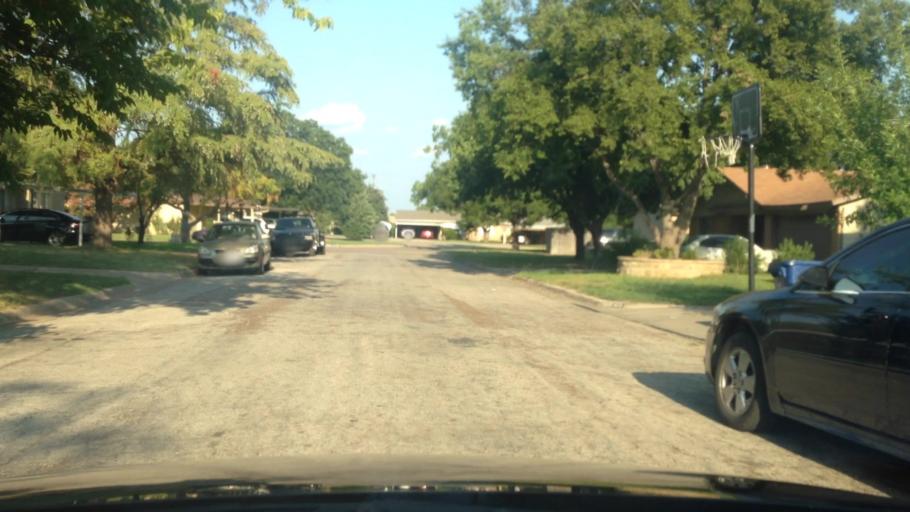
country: US
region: Texas
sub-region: Tarrant County
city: Everman
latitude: 32.6287
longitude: -97.2923
